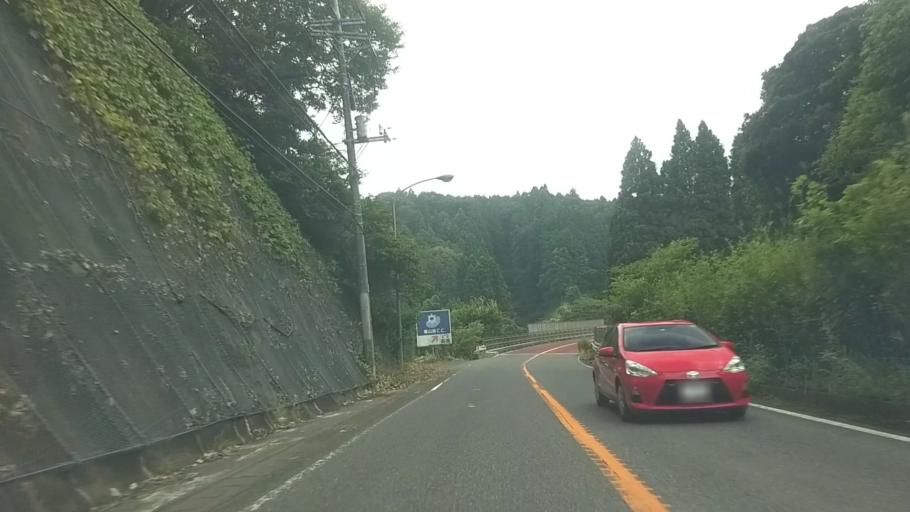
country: JP
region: Chiba
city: Kawaguchi
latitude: 35.2503
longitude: 140.0759
